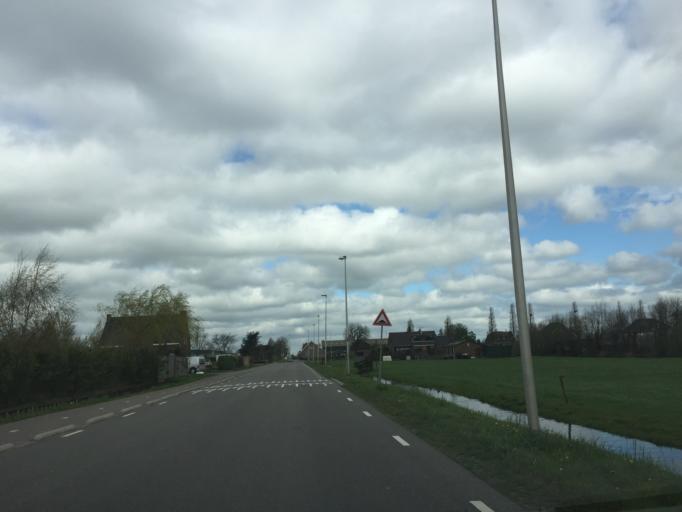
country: NL
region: South Holland
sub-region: Gemeente Boskoop
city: Boskoop
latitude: 52.0809
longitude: 4.6330
